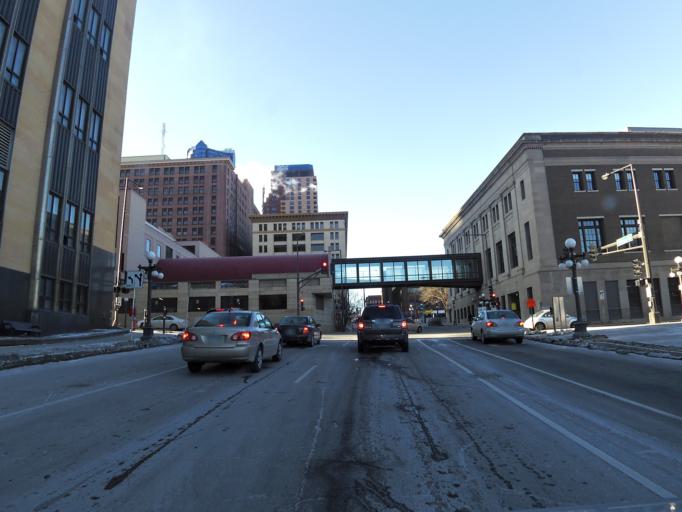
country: US
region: Minnesota
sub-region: Ramsey County
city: Saint Paul
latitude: 44.9467
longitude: -93.0866
